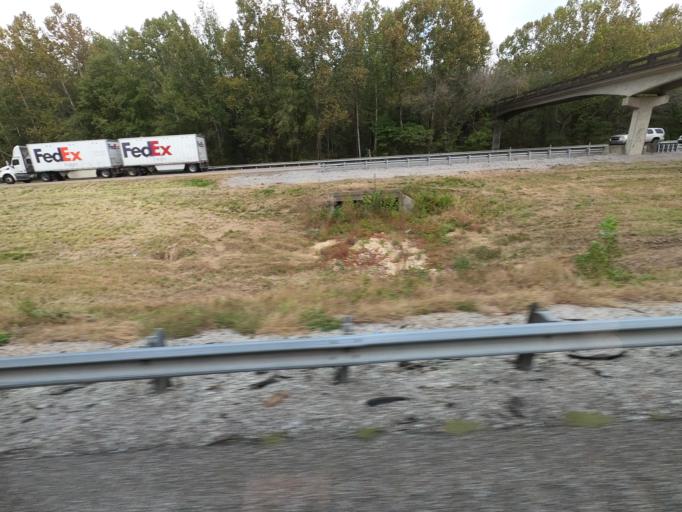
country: US
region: Tennessee
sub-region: Humphreys County
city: Waverly
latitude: 35.8775
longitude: -87.7469
